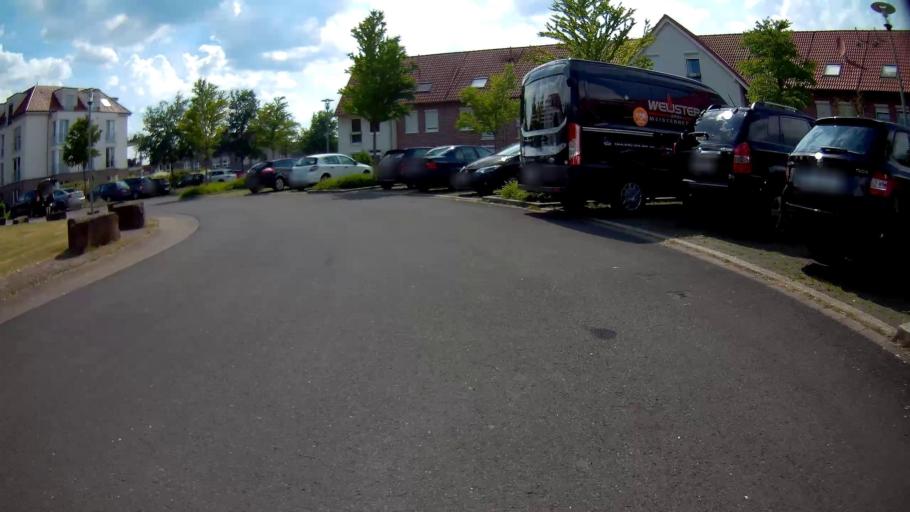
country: DE
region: North Rhine-Westphalia
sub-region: Regierungsbezirk Munster
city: Gladbeck
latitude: 51.5889
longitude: 6.9574
